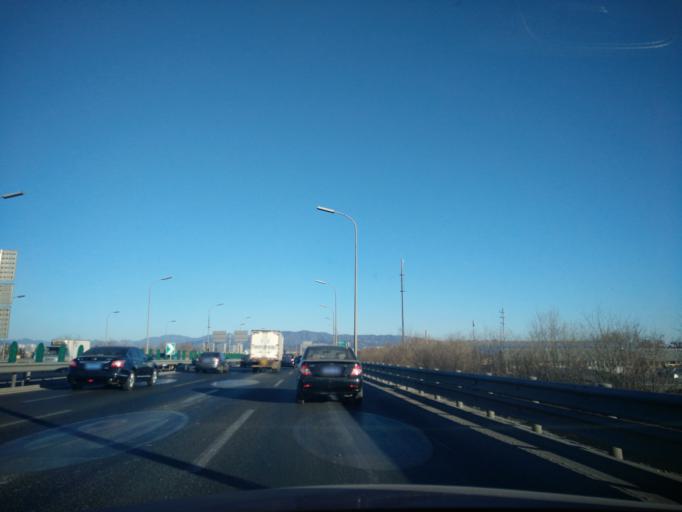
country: CN
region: Beijing
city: Lugu
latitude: 39.8707
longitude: 116.2036
